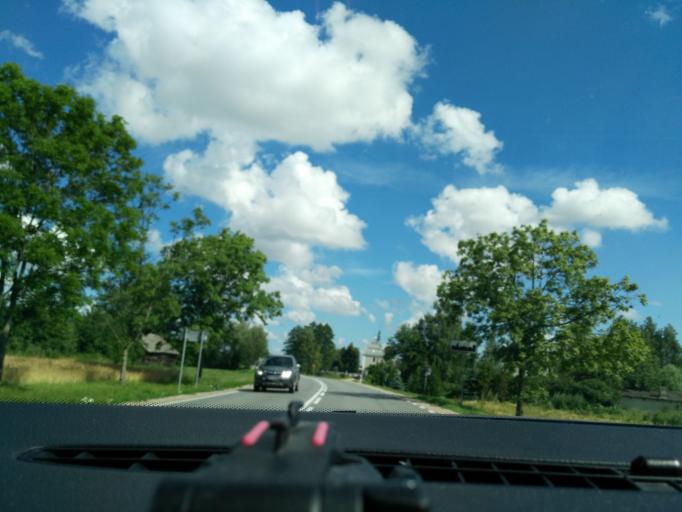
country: PL
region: Masovian Voivodeship
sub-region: Powiat losicki
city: Losice
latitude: 52.1006
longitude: 22.7468
